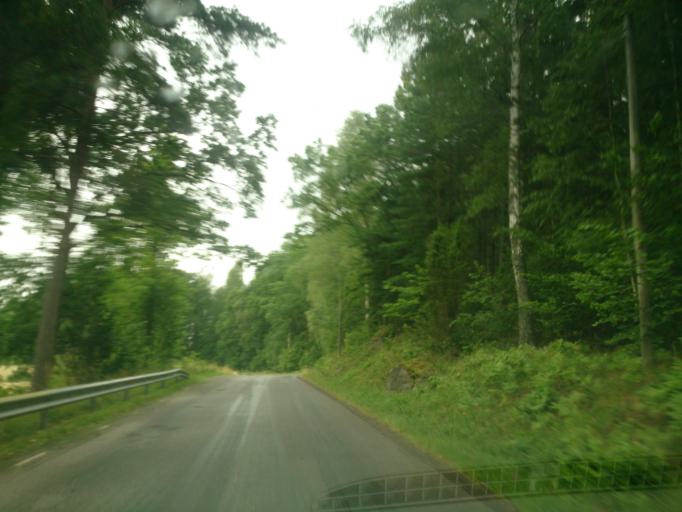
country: SE
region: OEstergoetland
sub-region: Atvidabergs Kommun
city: Atvidaberg
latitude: 58.2803
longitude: 16.1539
